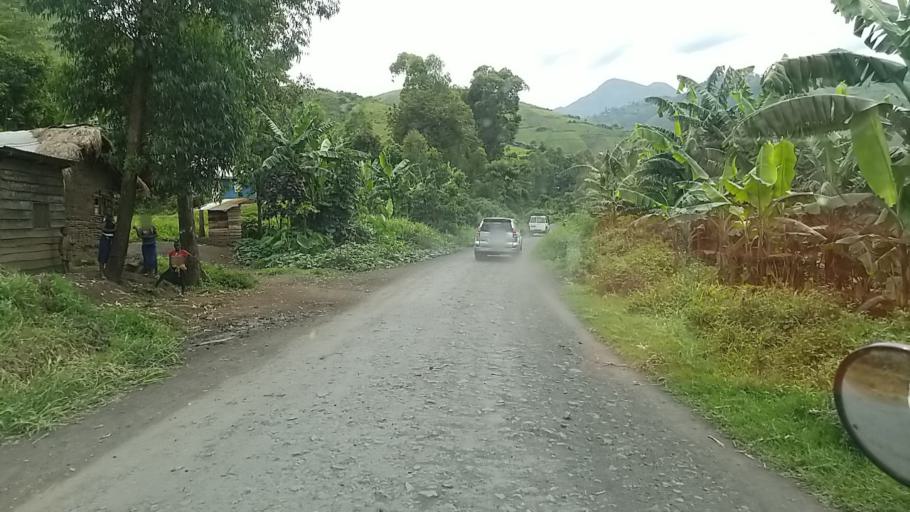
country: CD
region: Nord Kivu
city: Sake
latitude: -1.7408
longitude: 28.9975
